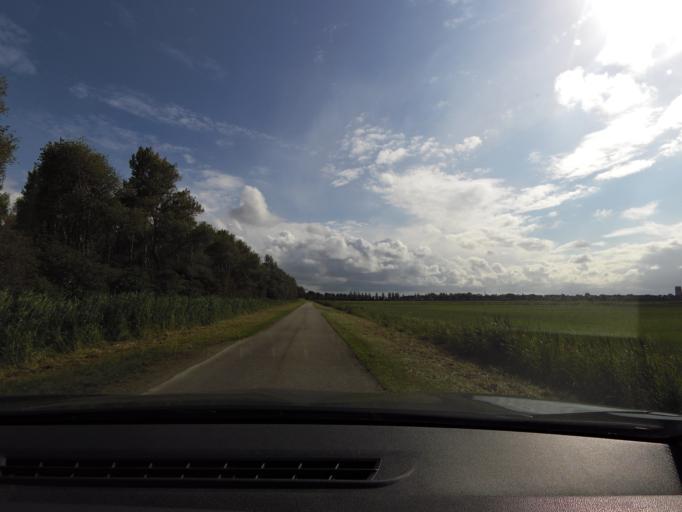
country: NL
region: South Holland
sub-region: Gemeente Goeree-Overflakkee
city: Goedereede
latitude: 51.8242
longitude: 3.9929
